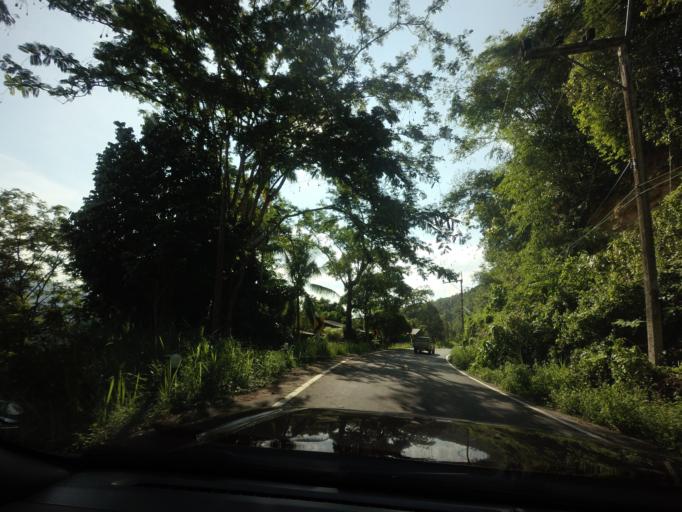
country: TH
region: Yala
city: Than To
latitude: 6.0792
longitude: 101.3333
